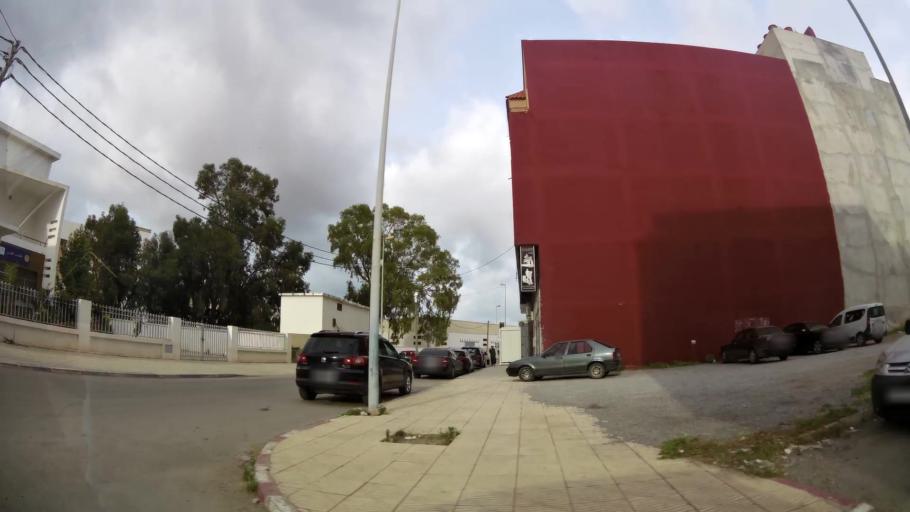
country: MA
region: Oriental
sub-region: Nador
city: Nador
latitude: 35.1560
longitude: -2.9279
